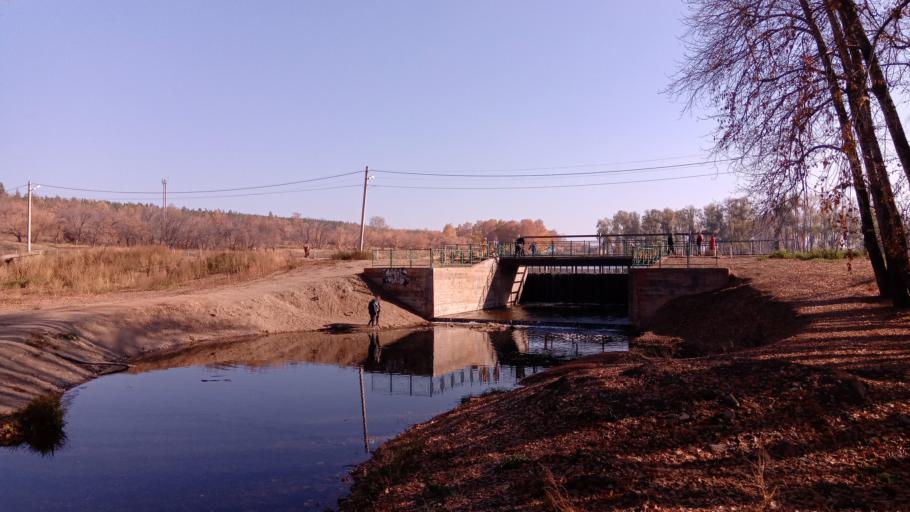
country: RU
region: Bashkortostan
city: Ishimbay
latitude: 53.4626
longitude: 56.0459
